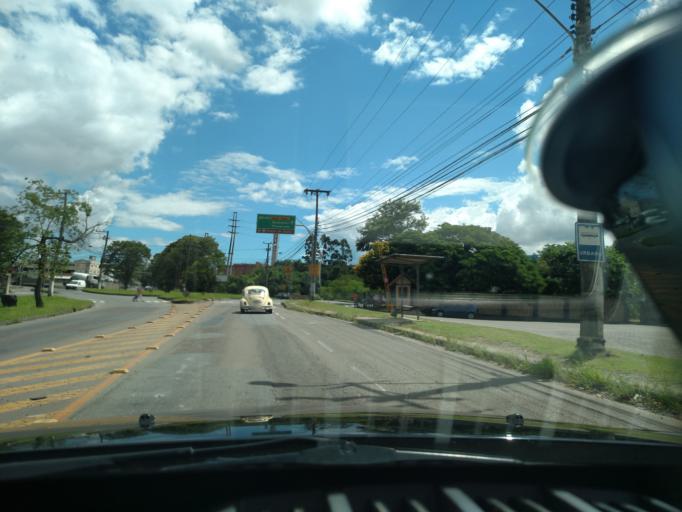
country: BR
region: Santa Catarina
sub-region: Blumenau
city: Blumenau
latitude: -26.8735
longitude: -49.1055
